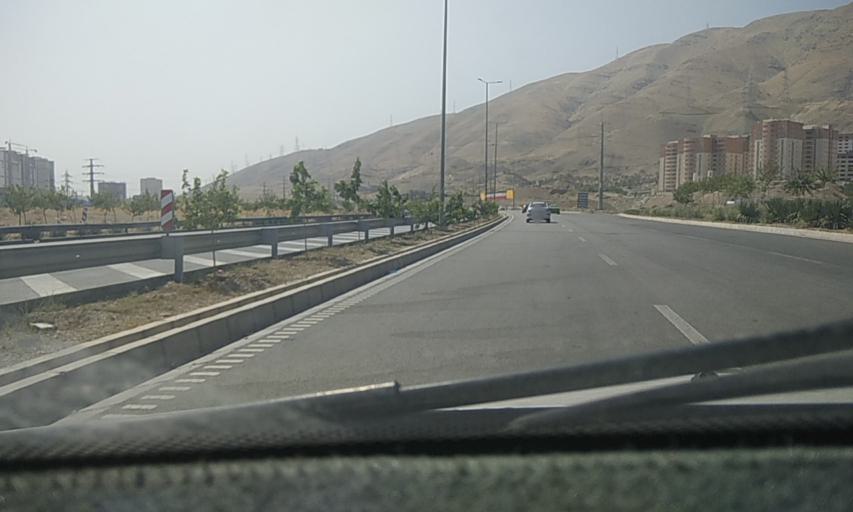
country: IR
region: Tehran
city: Shahr-e Qods
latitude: 35.7602
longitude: 51.1758
